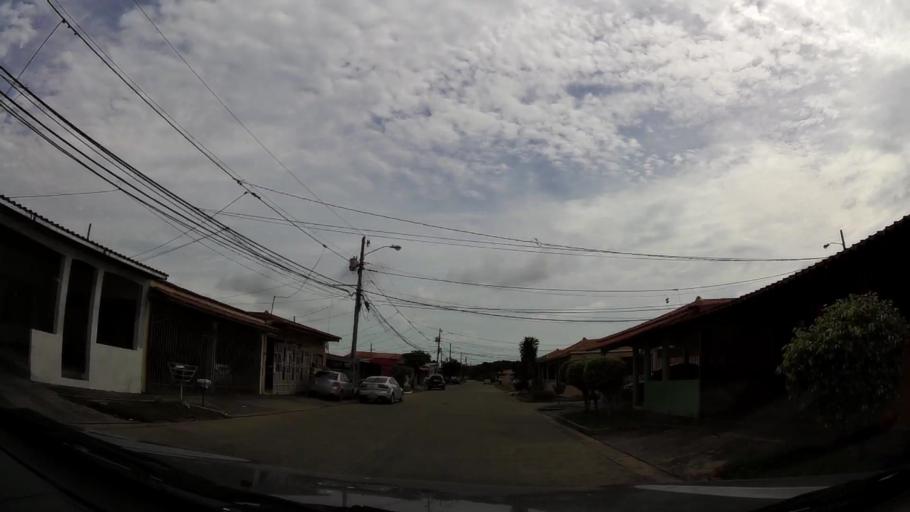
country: PA
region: Panama
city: Tocumen
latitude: 9.0415
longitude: -79.4097
